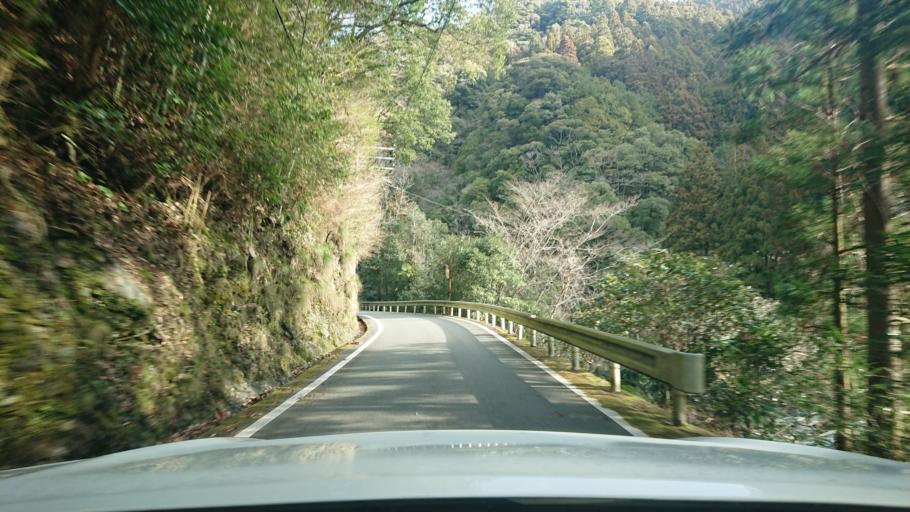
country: JP
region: Tokushima
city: Ishii
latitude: 33.8982
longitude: 134.3972
